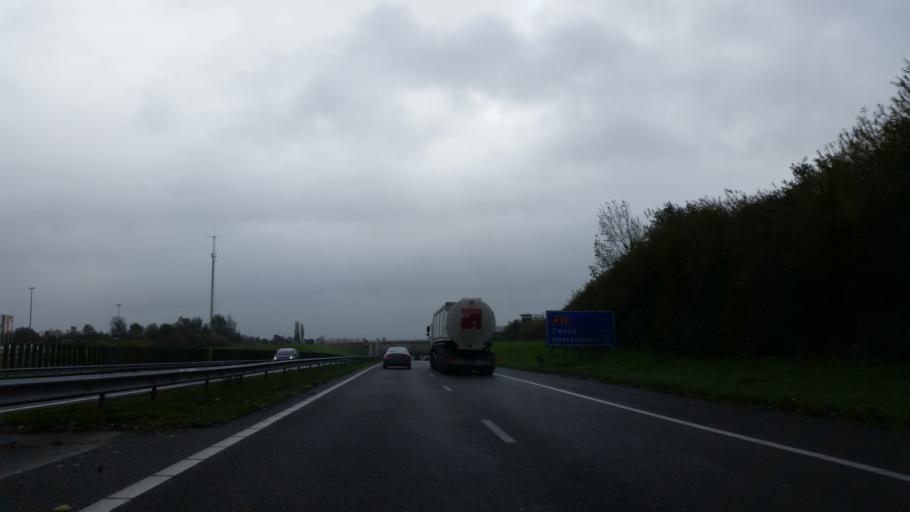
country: NL
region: Friesland
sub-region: Gemeente Boarnsterhim
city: Grou
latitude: 53.0833
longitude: 5.8266
